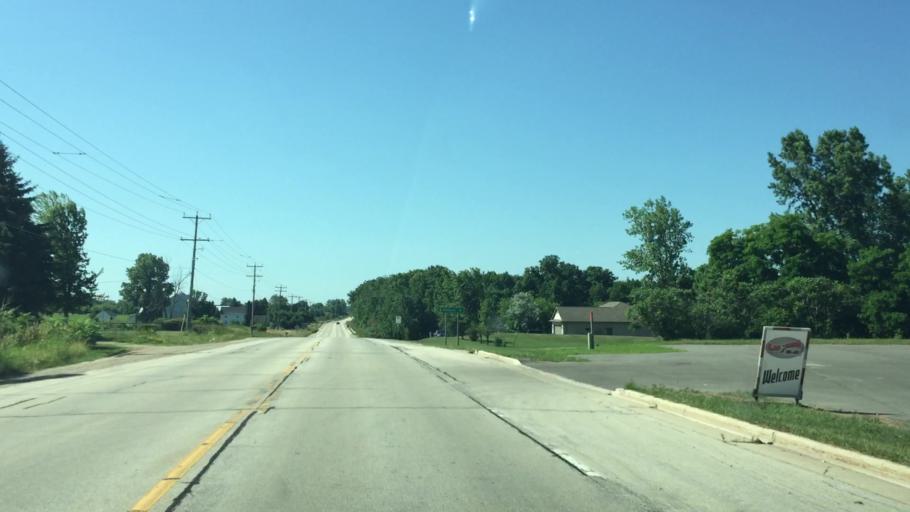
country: US
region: Wisconsin
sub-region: Calumet County
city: Sherwood
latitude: 44.1613
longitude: -88.2651
